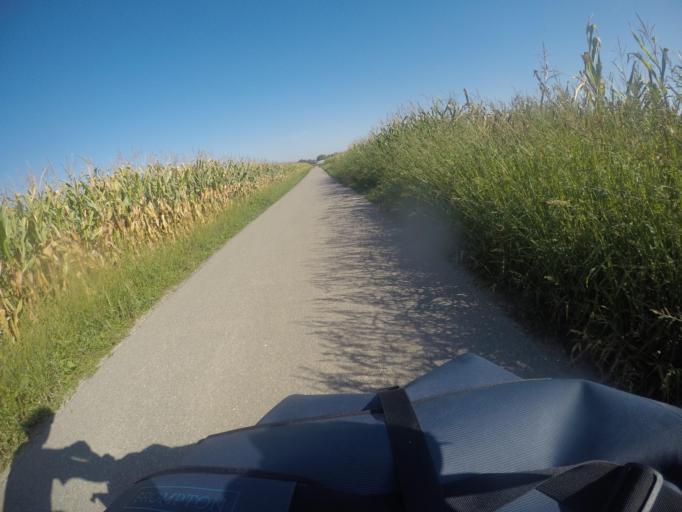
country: FR
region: Alsace
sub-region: Departement du Haut-Rhin
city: Ottmarsheim
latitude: 47.7748
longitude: 7.5056
